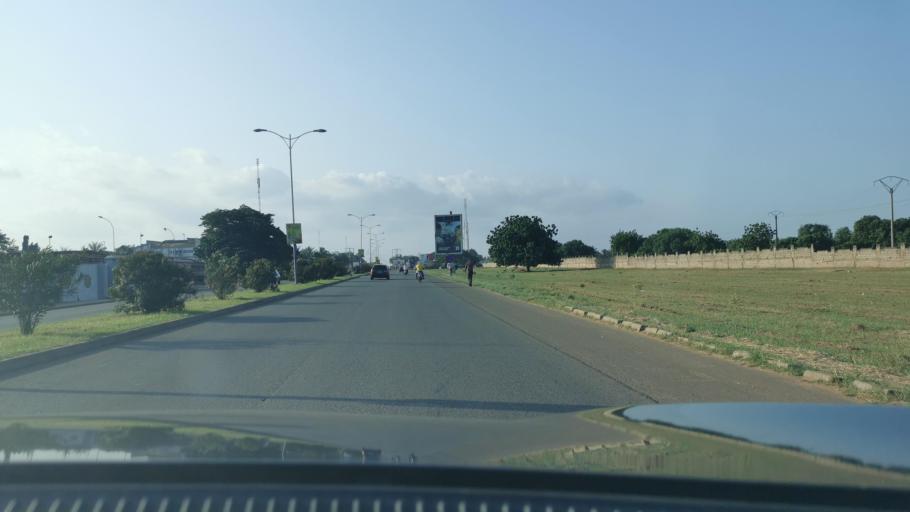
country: TG
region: Maritime
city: Lome
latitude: 6.2114
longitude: 1.2087
